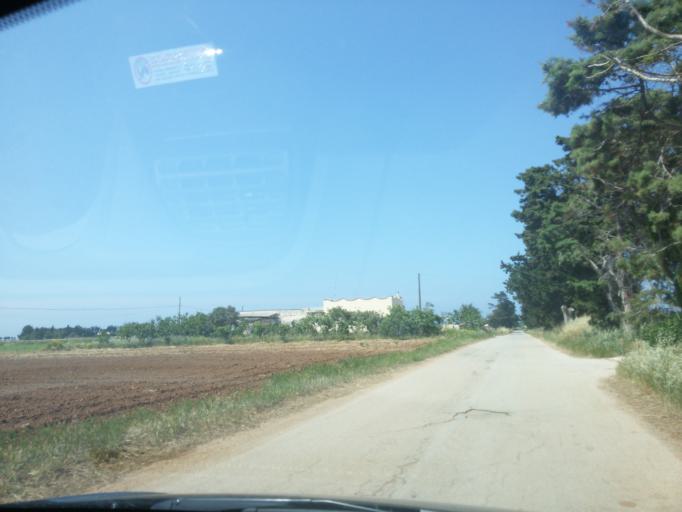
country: IT
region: Apulia
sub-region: Provincia di Brindisi
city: Brindisi
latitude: 40.6653
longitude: 17.8614
